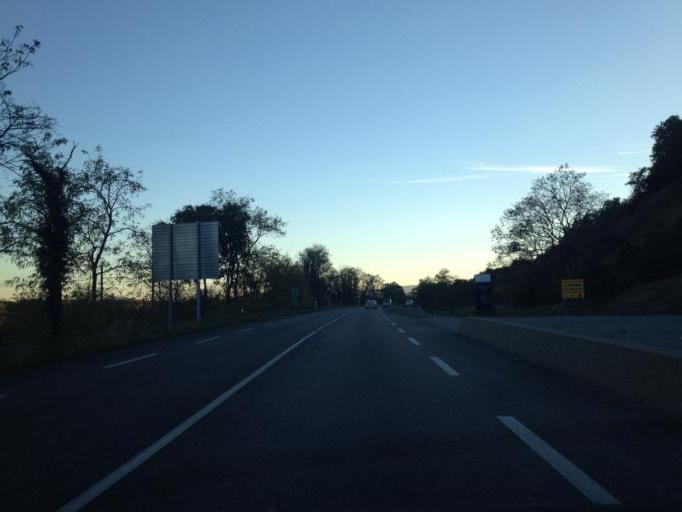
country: FR
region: Rhone-Alpes
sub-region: Departement de l'Ardeche
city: Rochemaure
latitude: 44.5957
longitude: 4.7135
